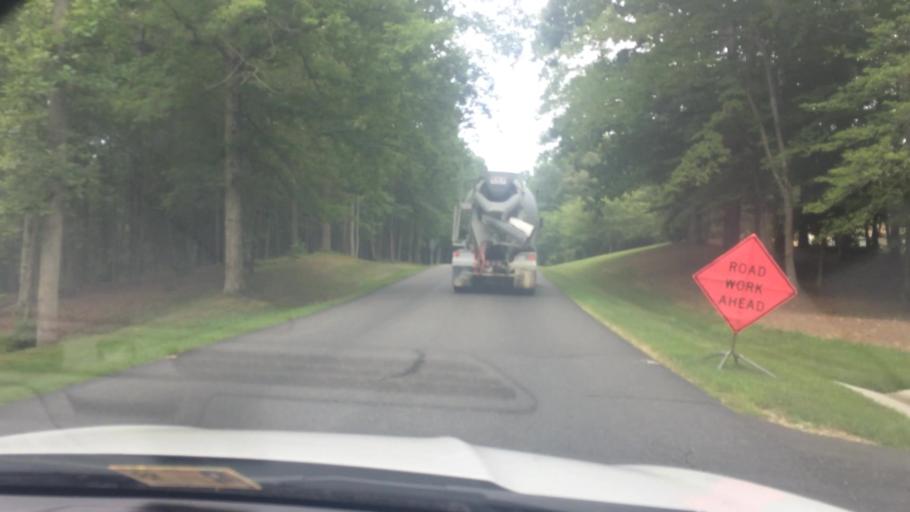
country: US
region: Virginia
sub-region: James City County
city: Williamsburg
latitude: 37.2934
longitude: -76.7919
